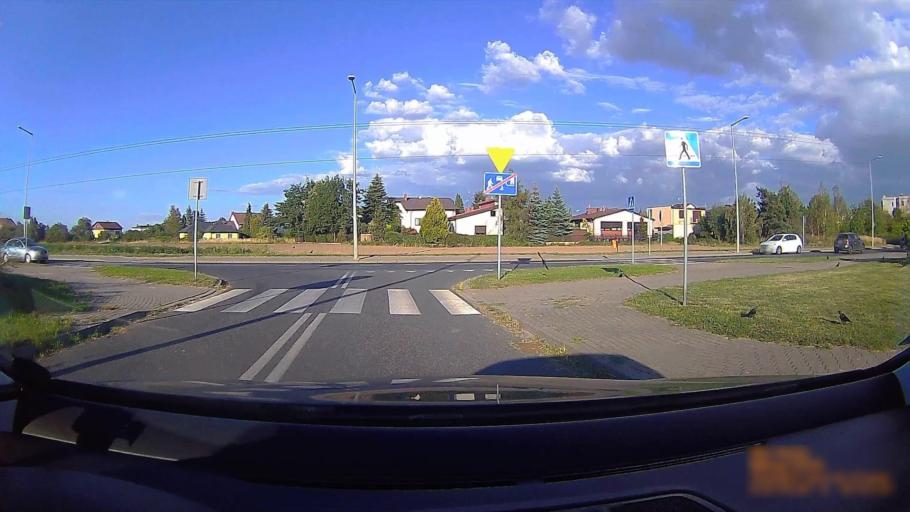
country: PL
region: Greater Poland Voivodeship
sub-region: Konin
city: Konin
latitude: 52.2011
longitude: 18.2384
